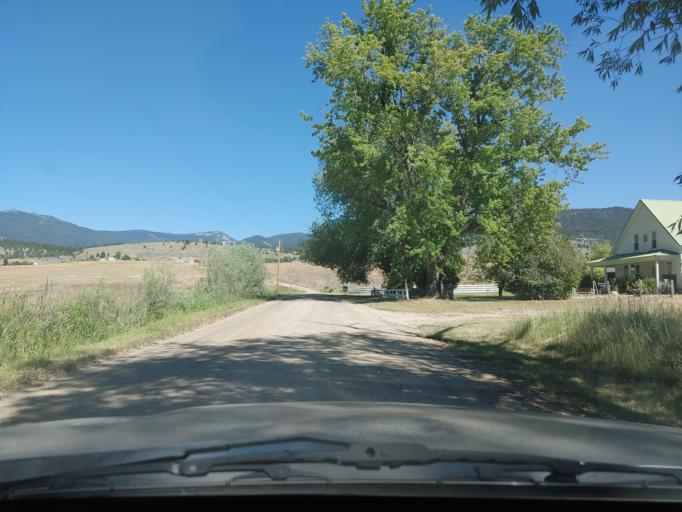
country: US
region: Montana
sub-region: Ravalli County
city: Hamilton
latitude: 46.2766
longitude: -114.0297
